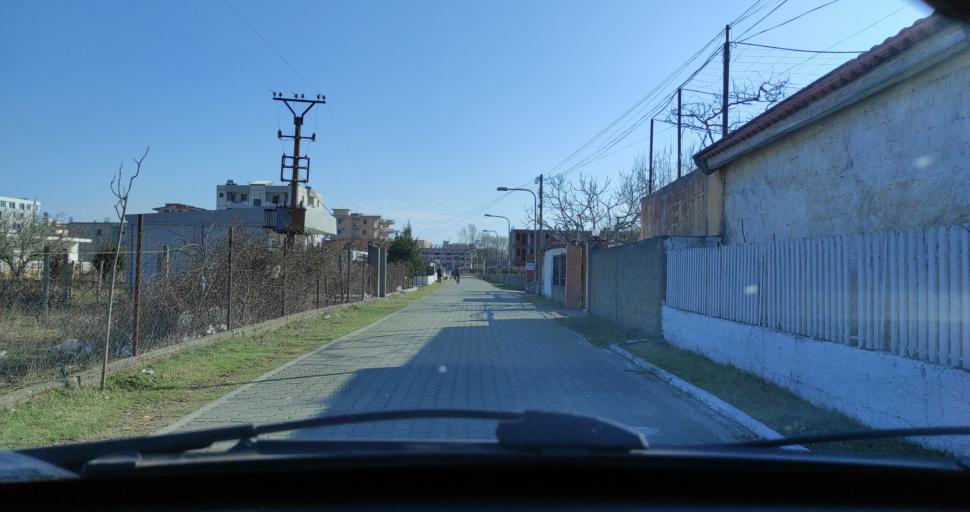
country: AL
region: Shkoder
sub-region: Rrethi i Shkodres
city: Velipoje
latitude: 41.8682
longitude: 19.4214
